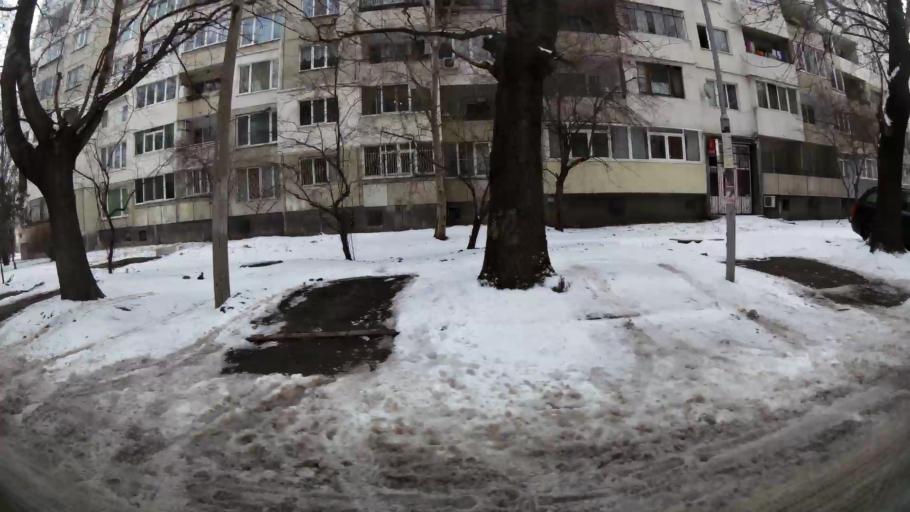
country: BG
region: Sofia-Capital
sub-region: Stolichna Obshtina
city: Sofia
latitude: 42.7135
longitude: 23.3019
